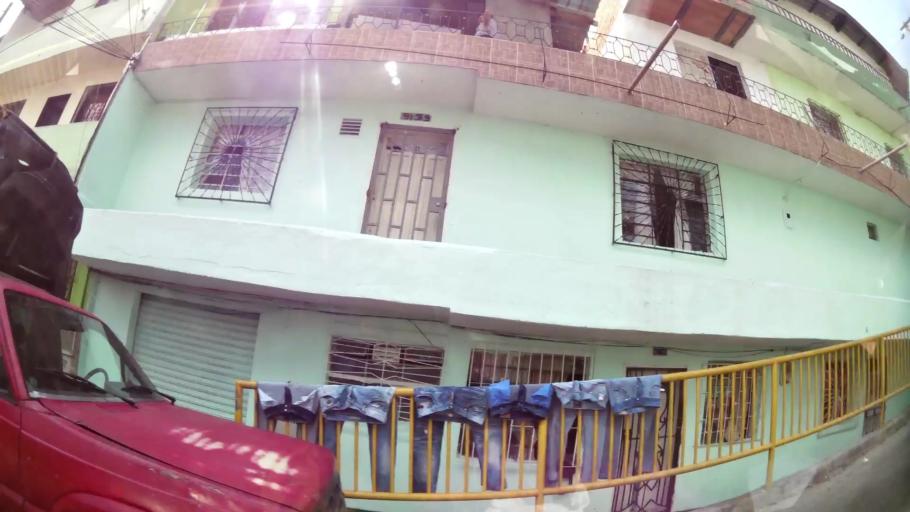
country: CO
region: Antioquia
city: Medellin
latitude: 6.2877
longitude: -75.5797
